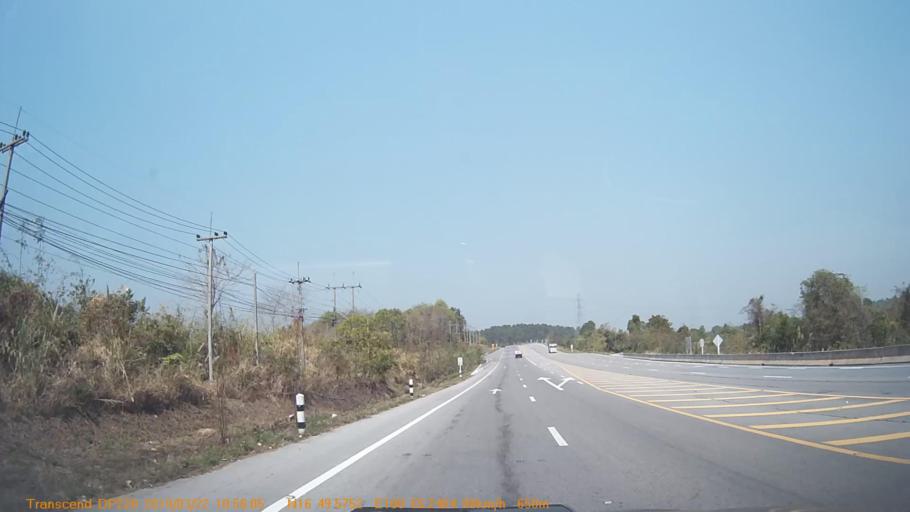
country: TH
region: Phetchabun
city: Khao Kho
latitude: 16.8264
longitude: 100.9205
